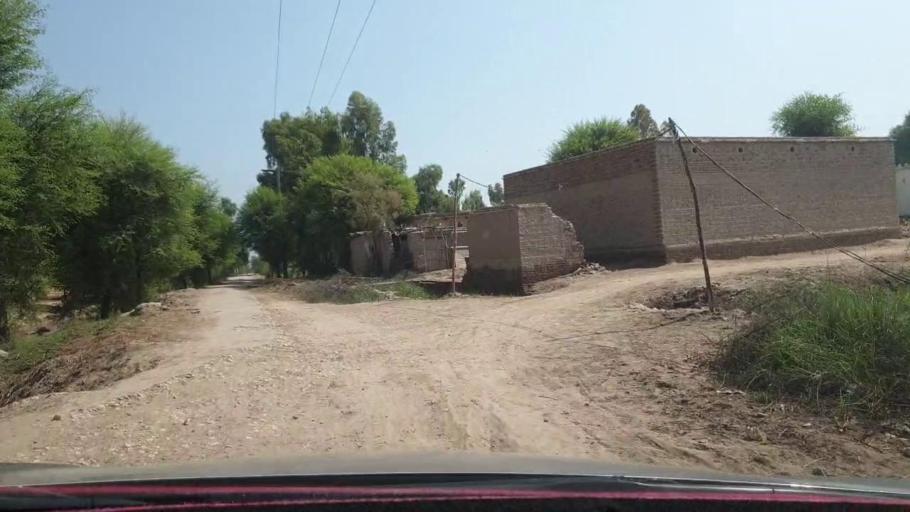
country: PK
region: Sindh
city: Warah
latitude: 27.4834
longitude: 67.8309
